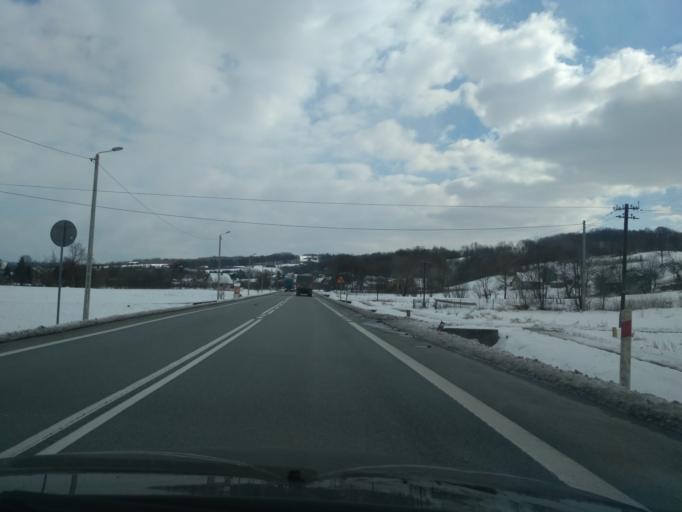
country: PL
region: Subcarpathian Voivodeship
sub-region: Powiat strzyzowski
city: Polomia
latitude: 49.9062
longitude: 21.8661
